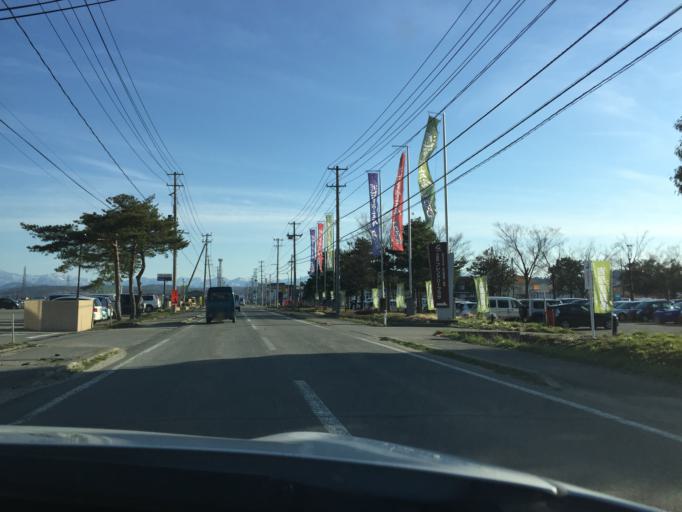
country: JP
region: Yamagata
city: Nagai
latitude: 38.0067
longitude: 140.0529
